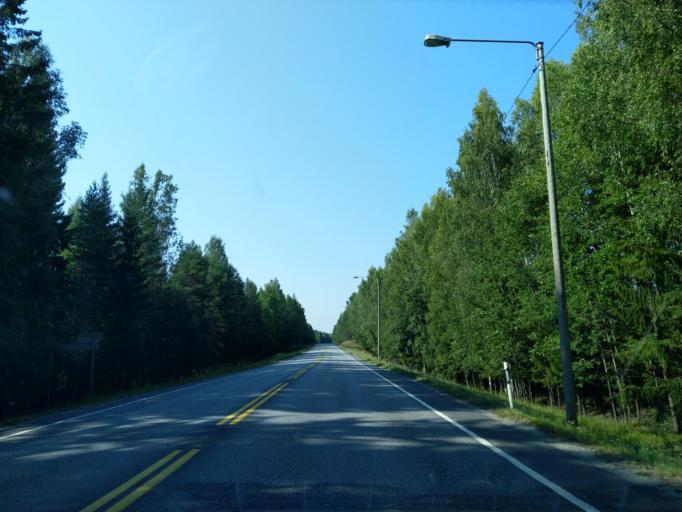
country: FI
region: Satakunta
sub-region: Pori
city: Pomarkku
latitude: 61.6484
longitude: 21.9548
